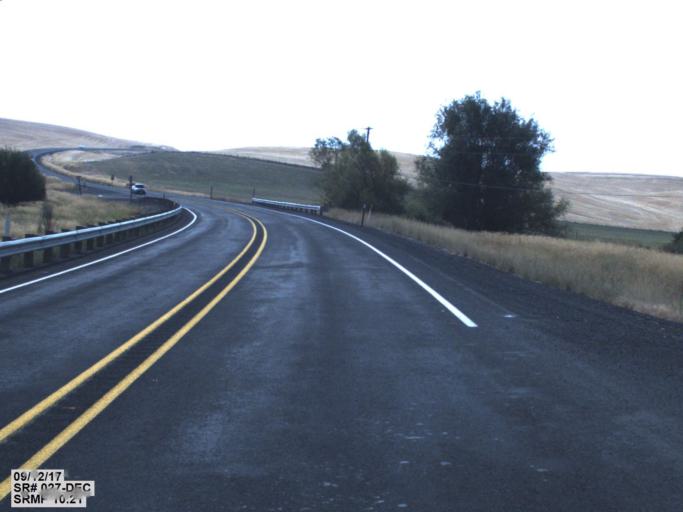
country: US
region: Washington
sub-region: Whitman County
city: Pullman
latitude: 46.8587
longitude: -117.1307
